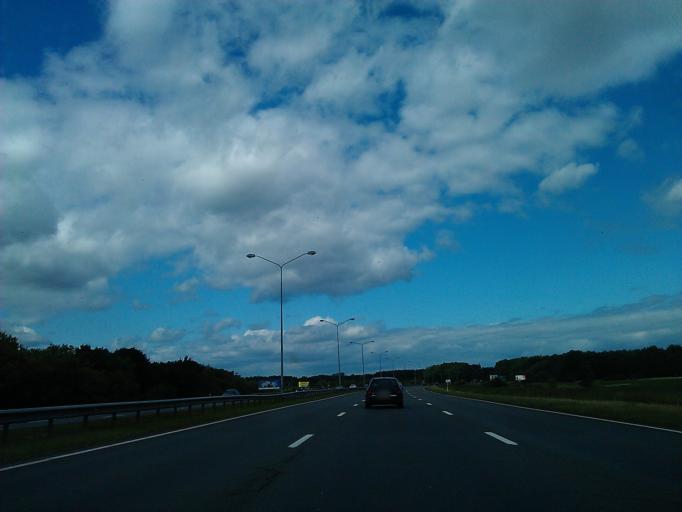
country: LV
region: Babite
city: Pinki
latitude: 56.9606
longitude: 23.8890
